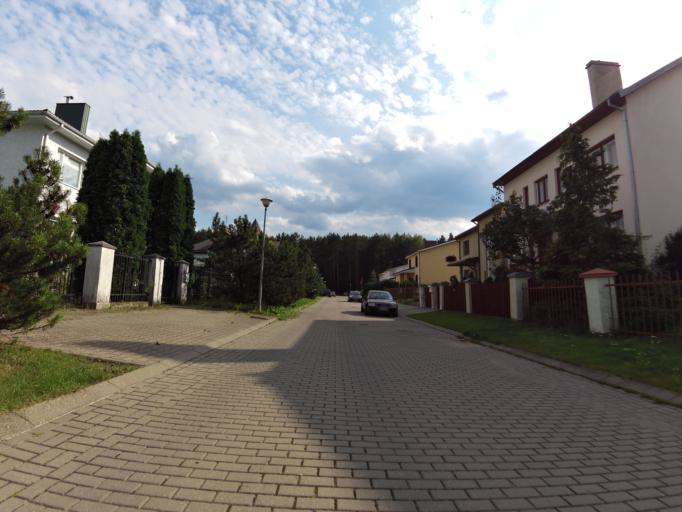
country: LT
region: Vilnius County
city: Lazdynai
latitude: 54.6659
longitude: 25.2185
